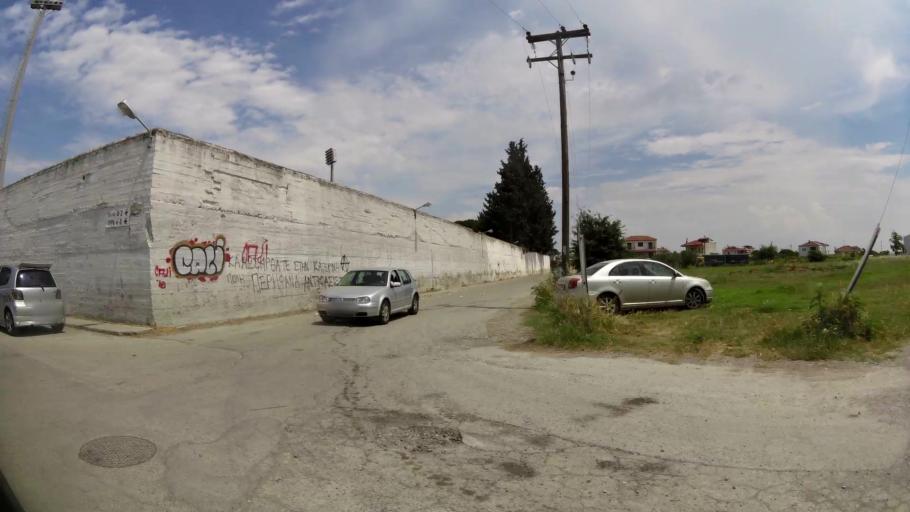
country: GR
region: Central Macedonia
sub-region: Nomos Pierias
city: Katerini
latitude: 40.2603
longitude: 22.5126
